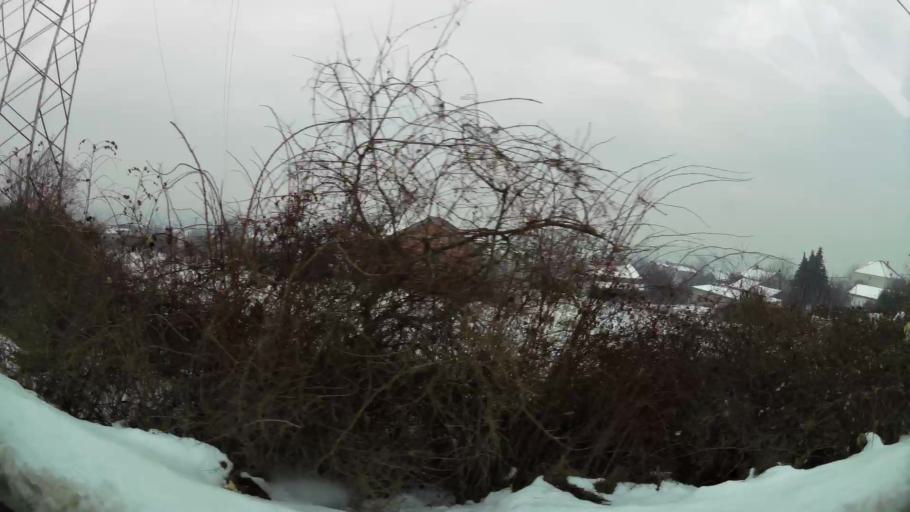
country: MK
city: Kondovo
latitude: 42.0386
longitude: 21.3440
